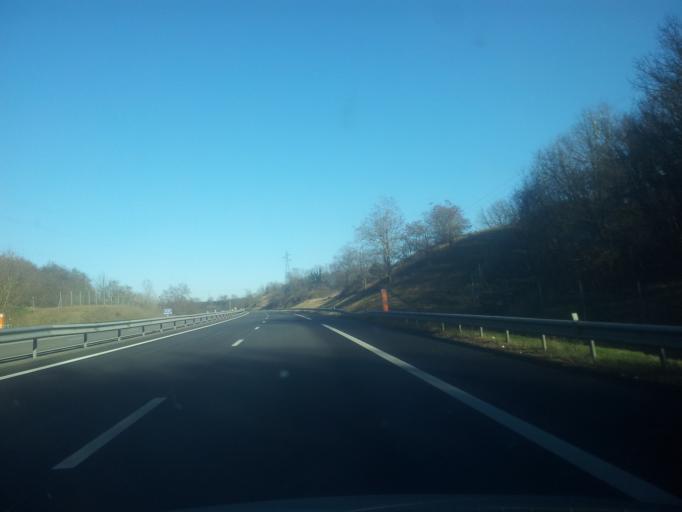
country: FR
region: Rhone-Alpes
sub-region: Departement de l'Isere
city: Saint-Hilaire-du-Rosier
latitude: 45.1057
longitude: 5.2510
